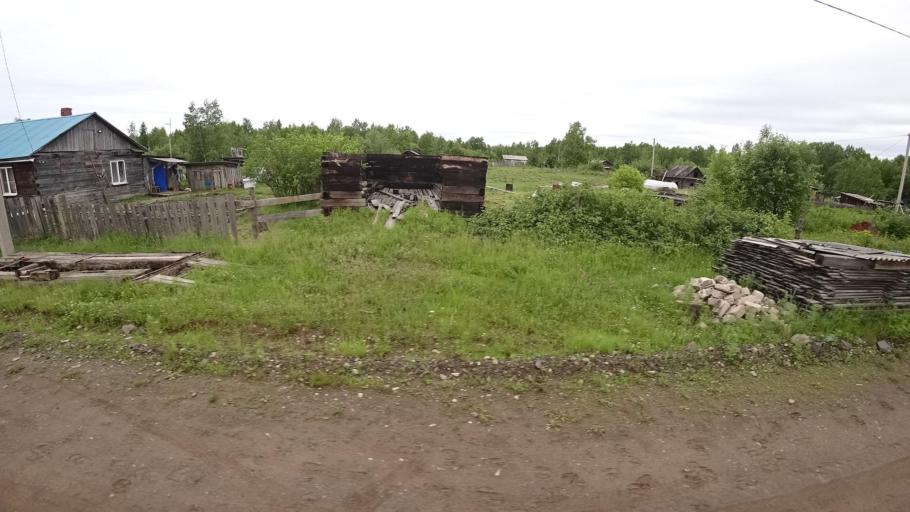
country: RU
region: Khabarovsk Krai
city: Amursk
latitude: 49.9168
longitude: 136.1631
